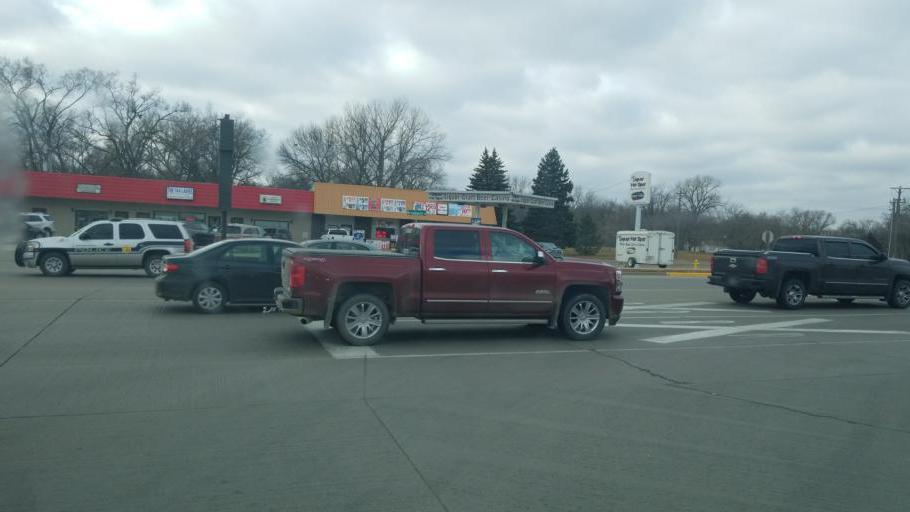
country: US
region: South Dakota
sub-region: Yankton County
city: Yankton
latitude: 42.8785
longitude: -97.3966
